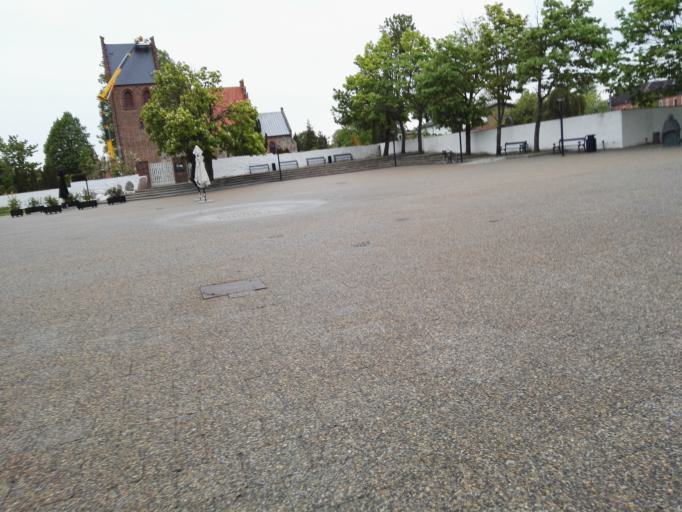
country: DK
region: Capital Region
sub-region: Ballerup Kommune
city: Ballerup
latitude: 55.7315
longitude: 12.3610
